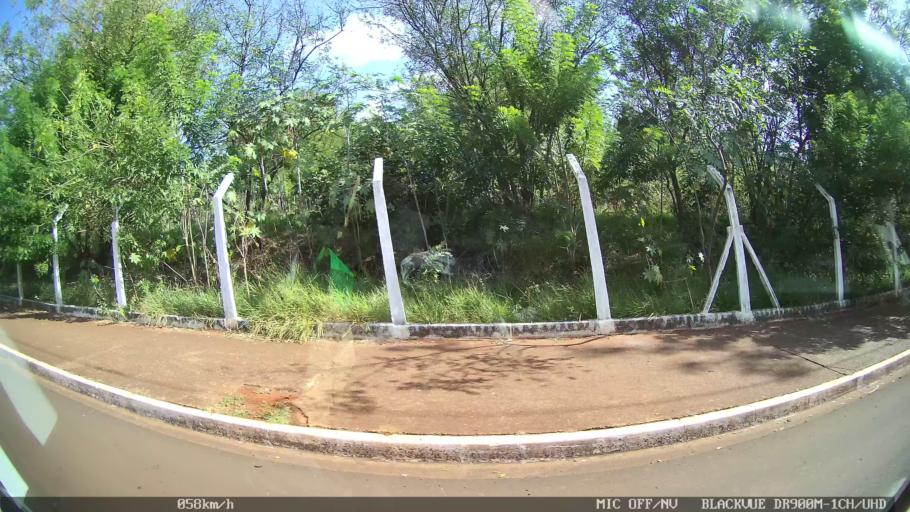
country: BR
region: Sao Paulo
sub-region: Ribeirao Preto
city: Ribeirao Preto
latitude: -21.1946
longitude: -47.8233
